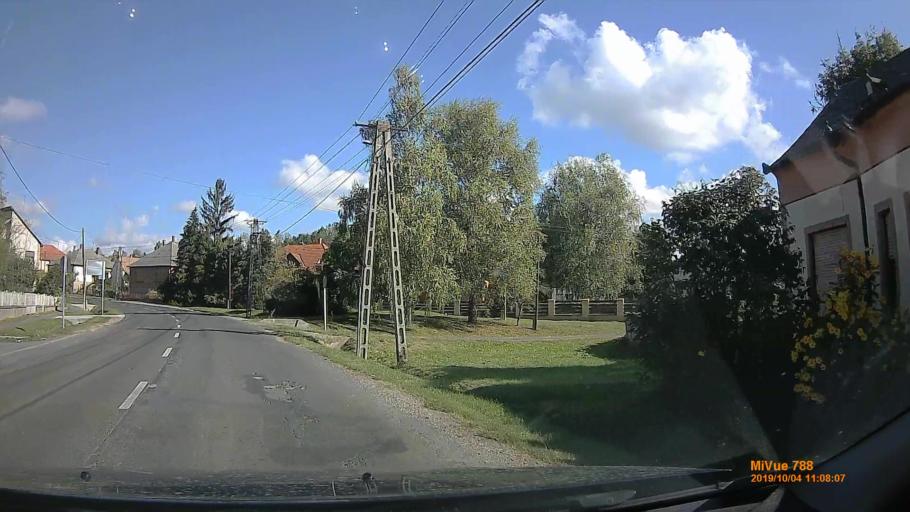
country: HU
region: Somogy
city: Kaposmero
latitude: 46.4071
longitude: 17.7371
